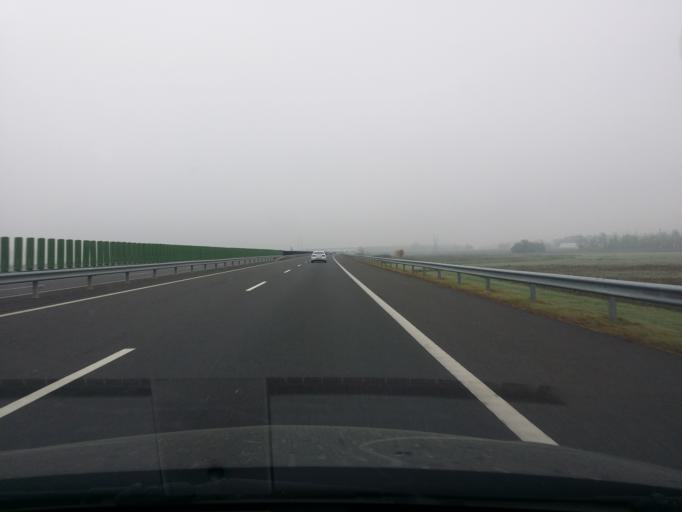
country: HU
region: Hajdu-Bihar
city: Hajdunanas
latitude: 47.8557
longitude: 21.3550
